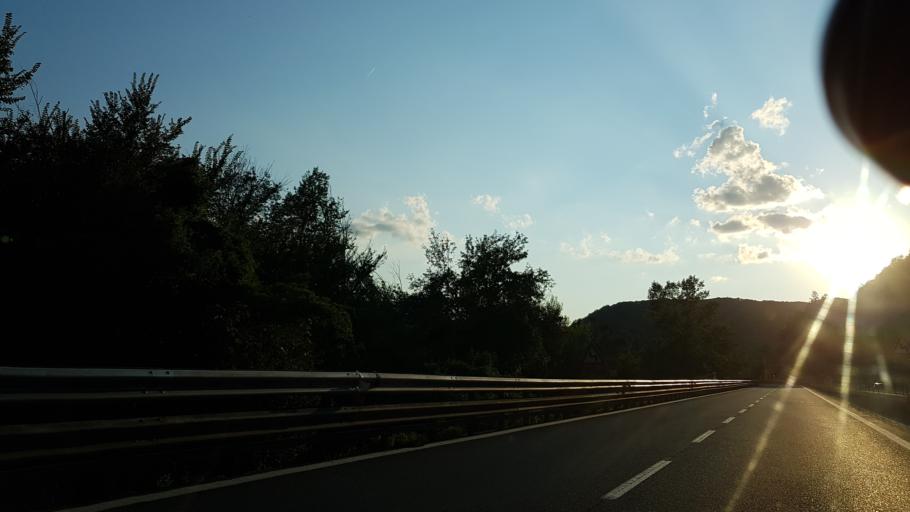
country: IT
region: Liguria
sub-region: Provincia di Genova
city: Borgo Fornari-Pieve
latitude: 44.5954
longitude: 8.9509
